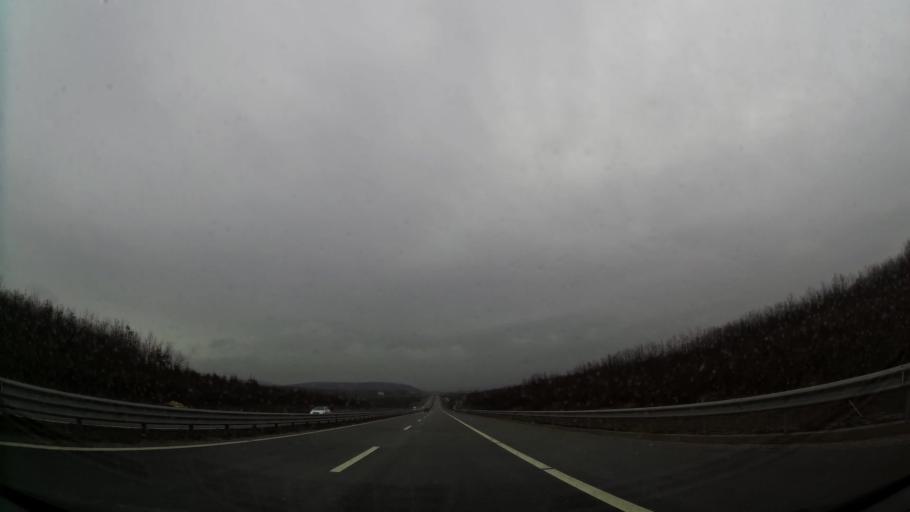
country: XK
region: Ferizaj
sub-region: Komuna e Ferizajt
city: Ferizaj
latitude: 42.3442
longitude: 21.2056
